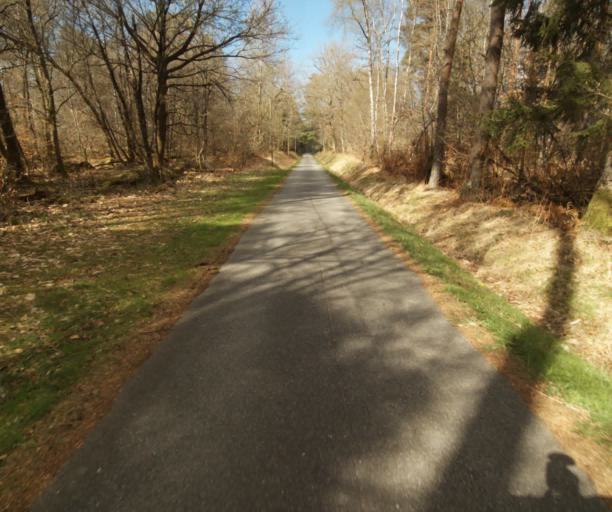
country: FR
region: Limousin
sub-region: Departement de la Correze
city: Laguenne
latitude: 45.2303
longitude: 1.9116
